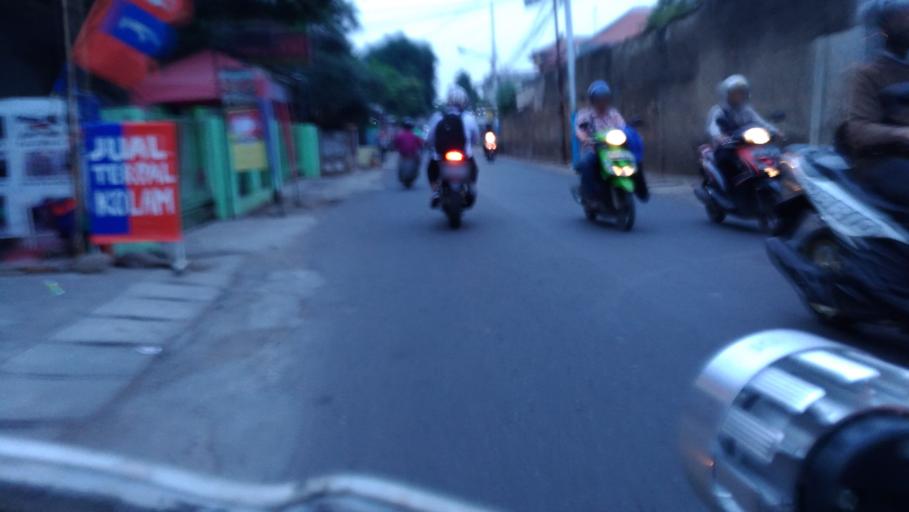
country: ID
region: West Java
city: Depok
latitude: -6.3639
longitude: 106.8853
